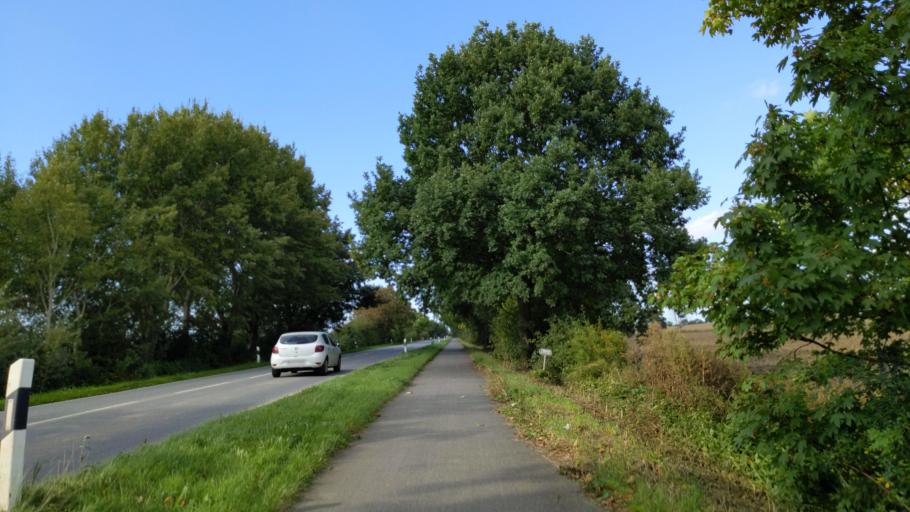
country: DE
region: Schleswig-Holstein
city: Stockelsdorf
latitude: 53.9378
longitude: 10.6318
